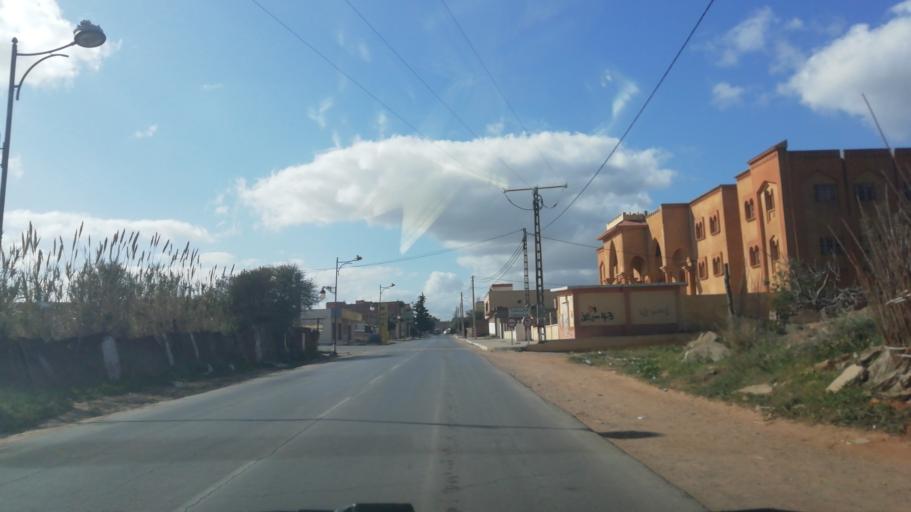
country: DZ
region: Relizane
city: Mazouna
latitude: 36.2748
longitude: 0.6350
